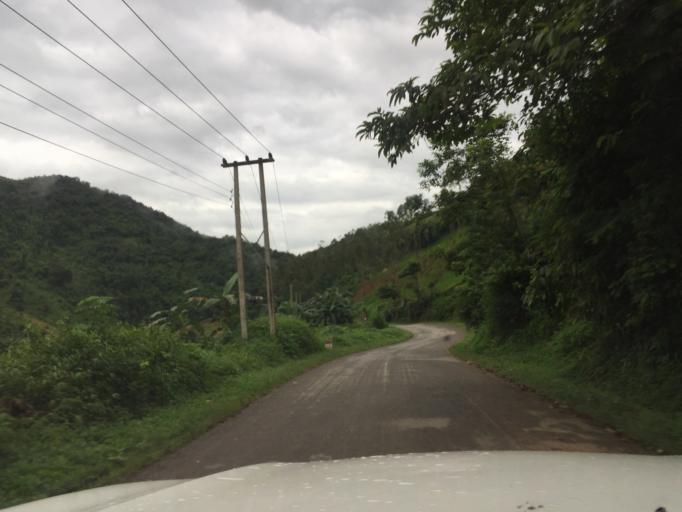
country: LA
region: Oudomxai
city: Muang La
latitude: 20.9551
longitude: 102.2158
